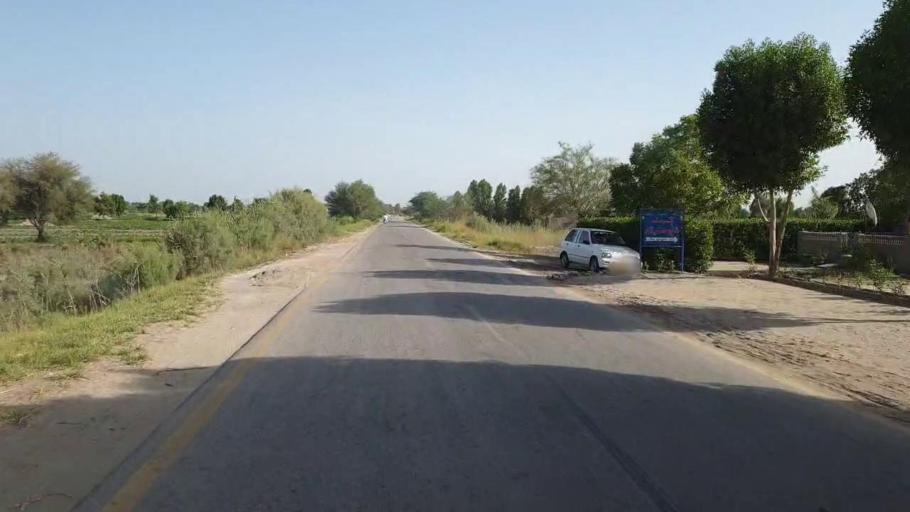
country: PK
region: Sindh
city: Daur
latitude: 26.4546
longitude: 68.4506
